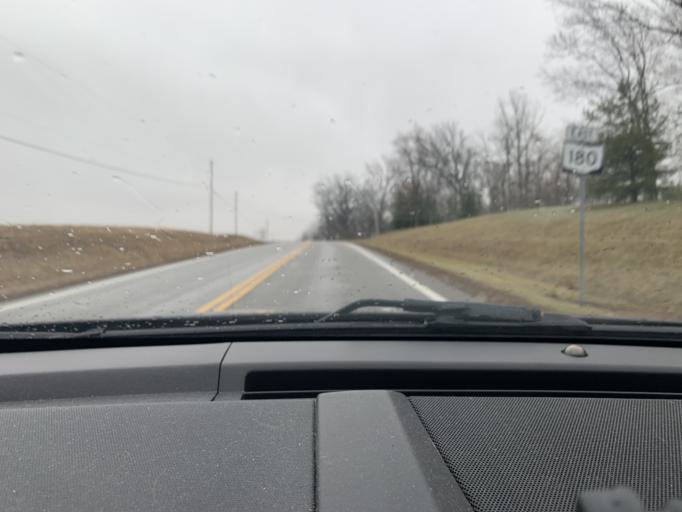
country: US
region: Ohio
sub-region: Ross County
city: Kingston
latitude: 39.4332
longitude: -82.8981
